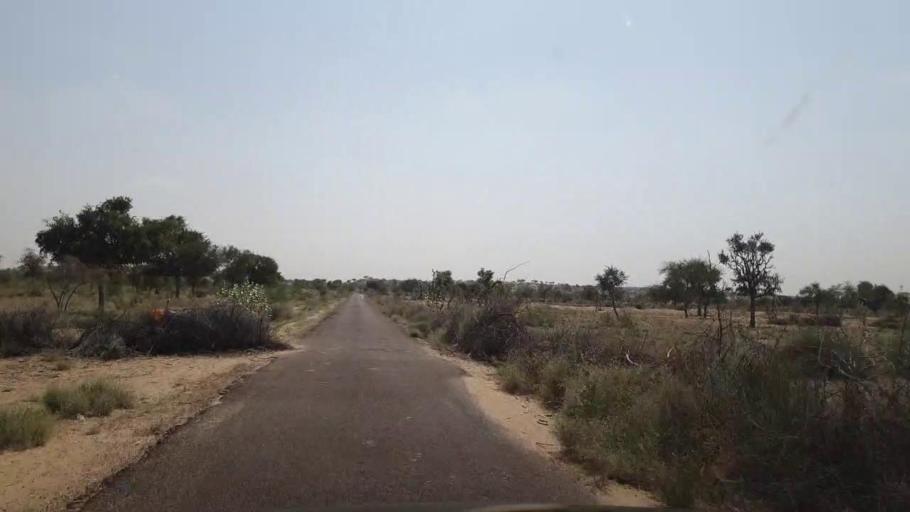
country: PK
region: Sindh
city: Islamkot
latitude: 25.0876
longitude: 70.7342
